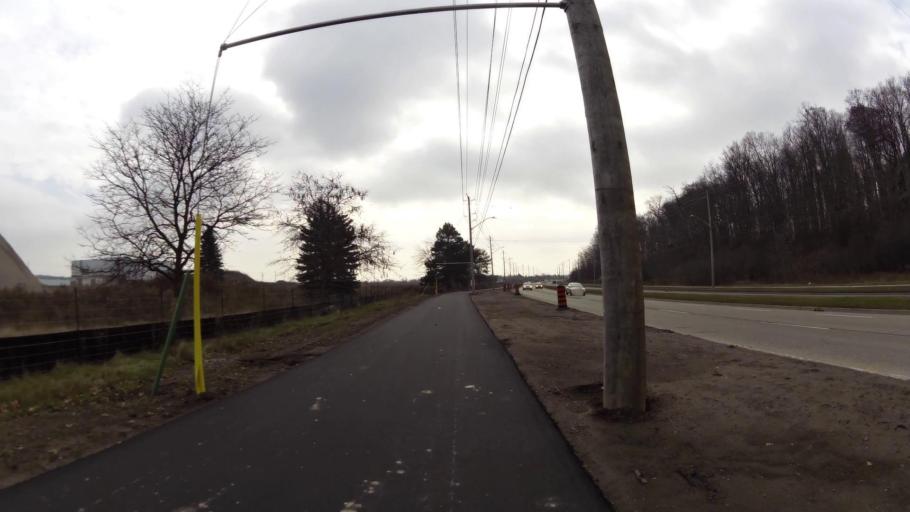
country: CA
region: Ontario
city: Kitchener
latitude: 43.4082
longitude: -80.4592
